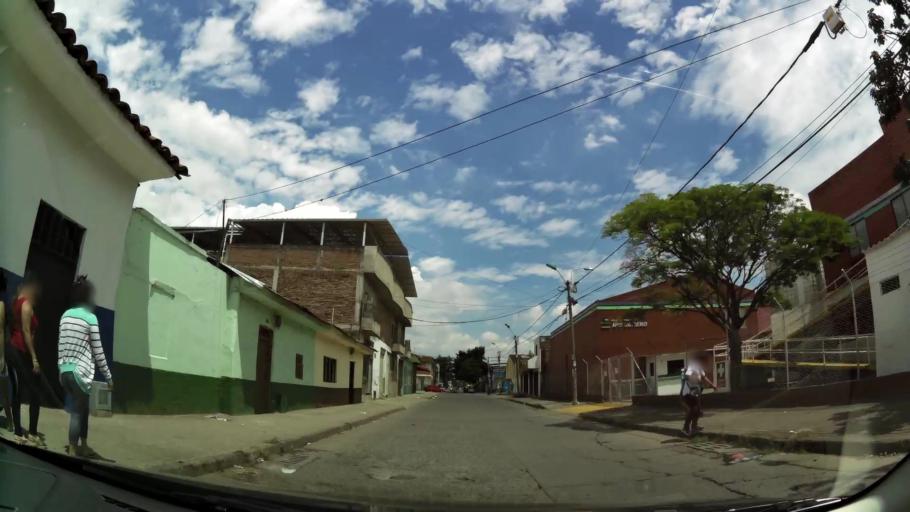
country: CO
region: Valle del Cauca
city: Cali
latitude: 3.4476
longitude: -76.5198
